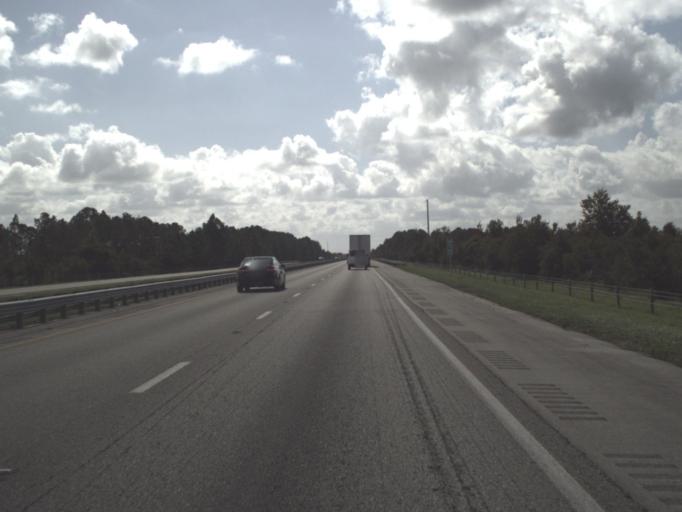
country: US
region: Florida
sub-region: Brevard County
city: June Park
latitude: 27.9072
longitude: -81.0487
